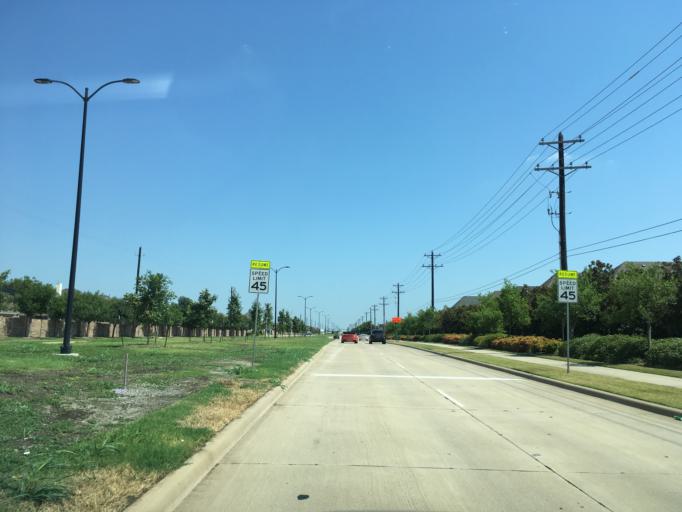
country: US
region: Texas
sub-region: Collin County
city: Frisco
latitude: 33.1796
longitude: -96.7679
